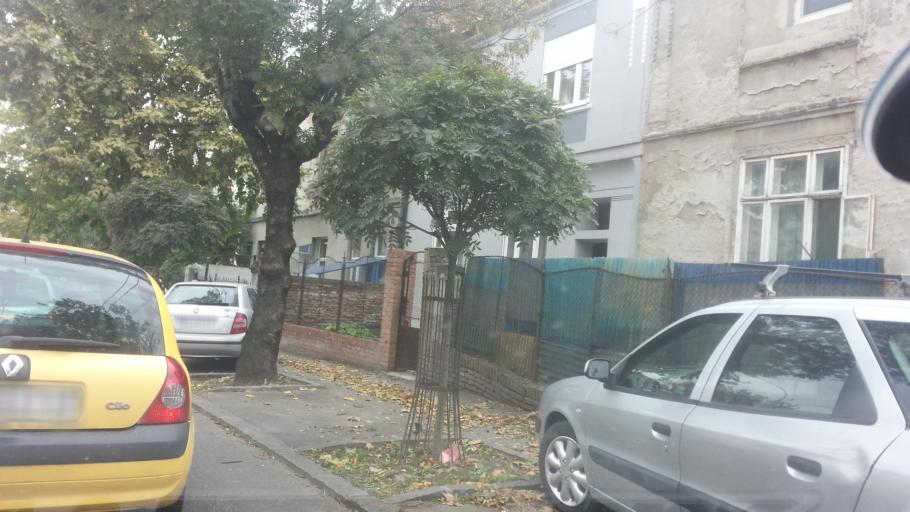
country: RS
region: Central Serbia
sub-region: Belgrade
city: Zemun
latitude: 44.8413
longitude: 20.4028
